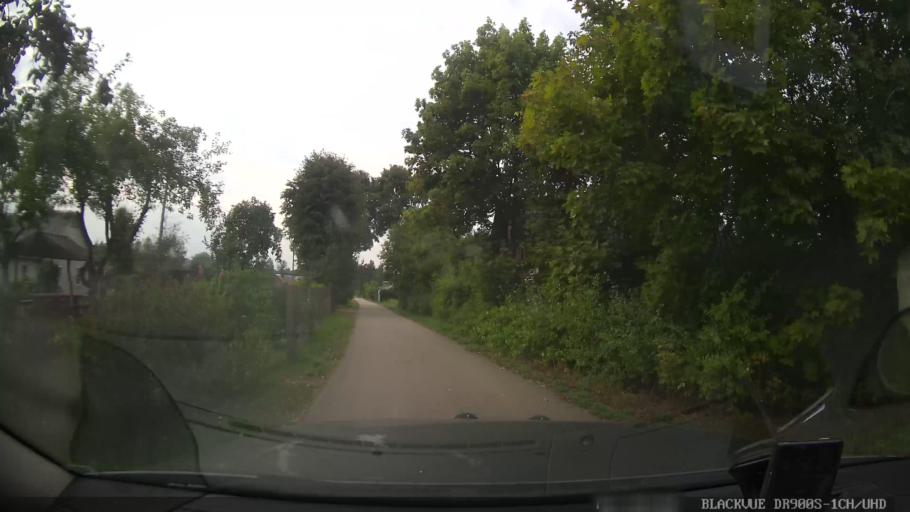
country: BY
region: Grodnenskaya
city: Ashmyany
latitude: 54.5310
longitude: 25.6692
